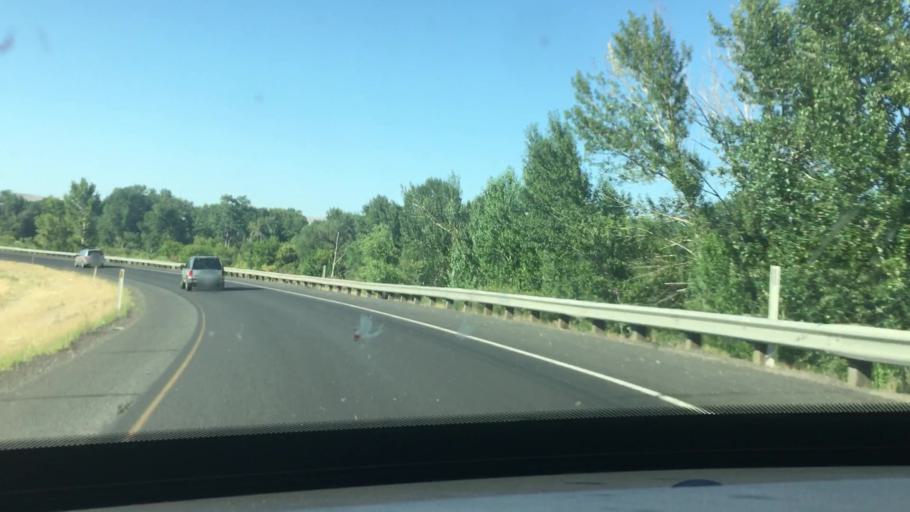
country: US
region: Washington
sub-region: Yakima County
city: Union Gap
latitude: 46.5418
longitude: -120.4697
